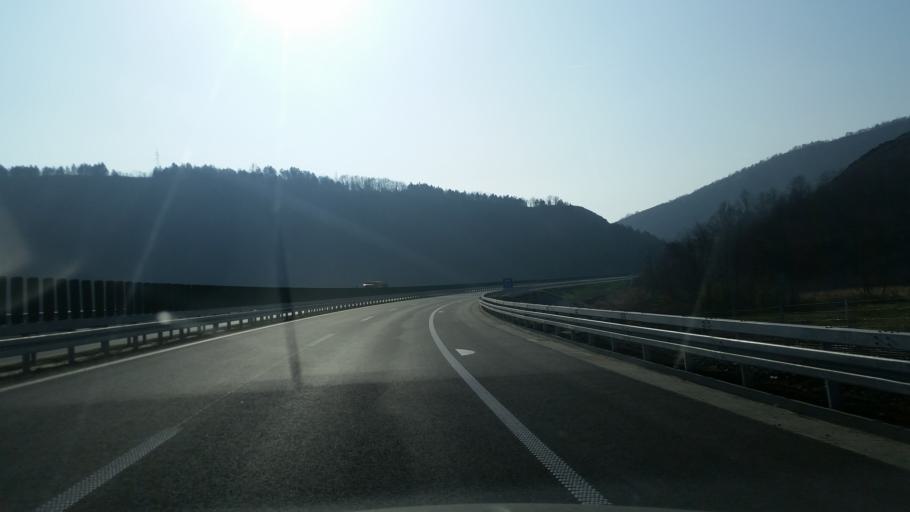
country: RS
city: Prislonica
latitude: 43.9972
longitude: 20.4035
